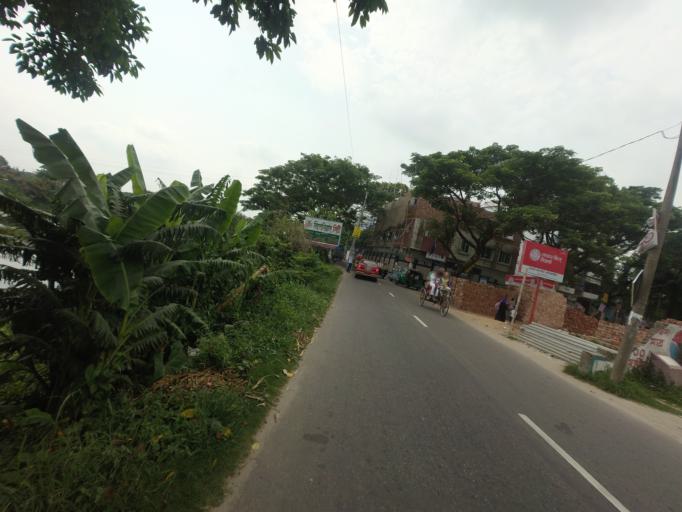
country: BD
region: Dhaka
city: Azimpur
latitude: 23.7227
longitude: 90.3455
